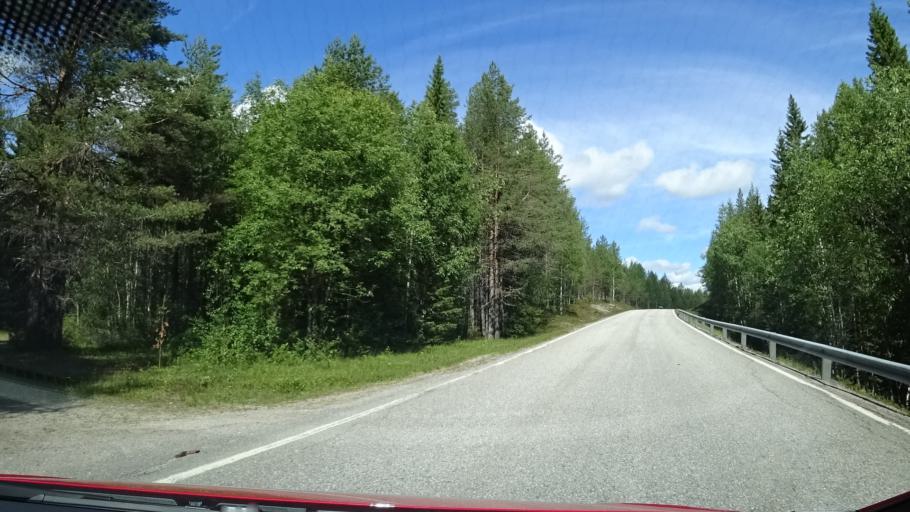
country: FI
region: Kainuu
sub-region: Kehys-Kainuu
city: Kuhmo
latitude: 64.7011
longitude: 29.6744
